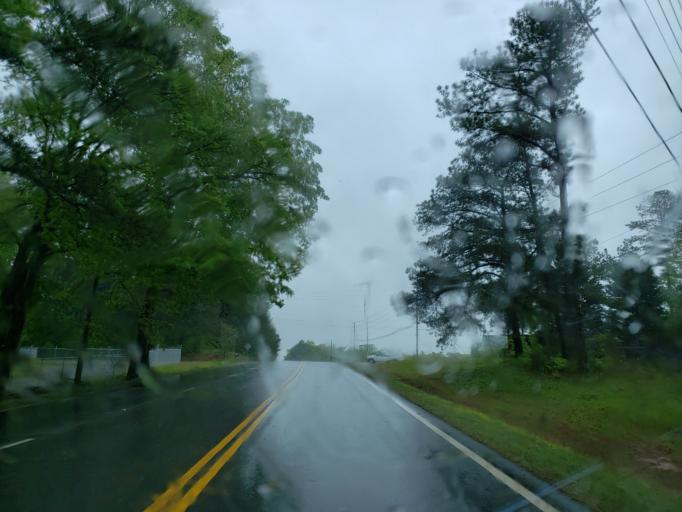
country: US
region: Georgia
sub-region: Carroll County
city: Temple
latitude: 33.7368
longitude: -84.9895
